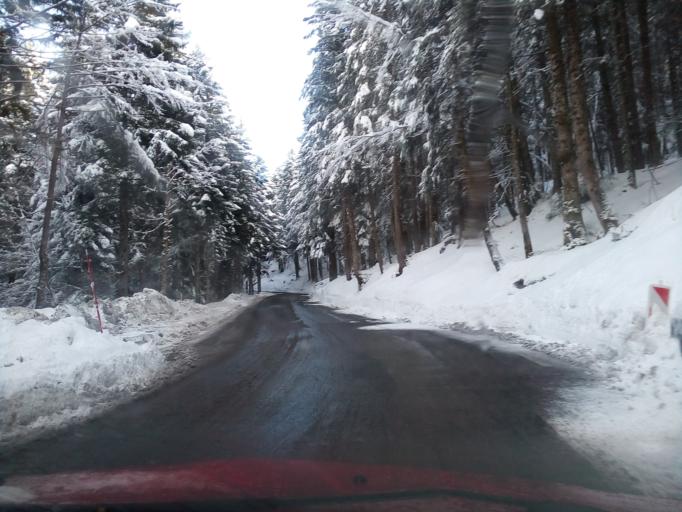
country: FR
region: Rhone-Alpes
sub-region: Departement de l'Isere
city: Le Sappey-en-Chartreuse
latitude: 45.3095
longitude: 5.7696
